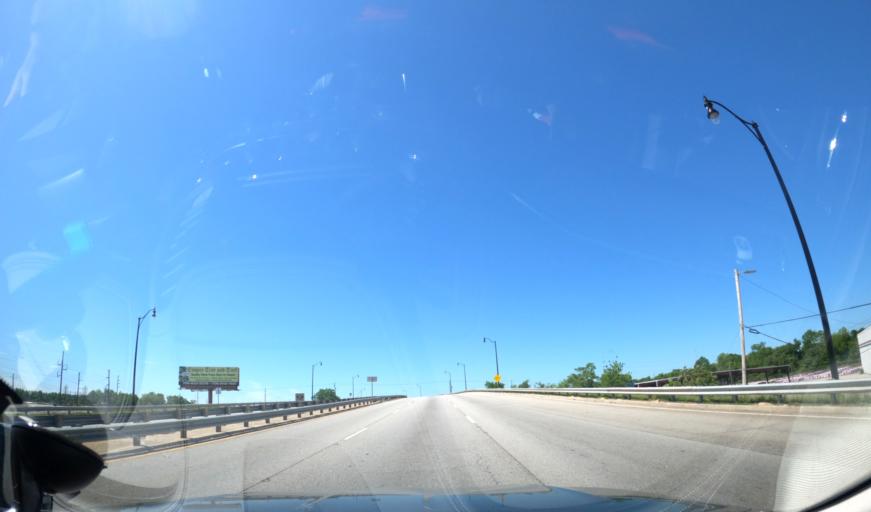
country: US
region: Georgia
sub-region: Richmond County
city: Augusta
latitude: 33.4624
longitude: -81.9651
